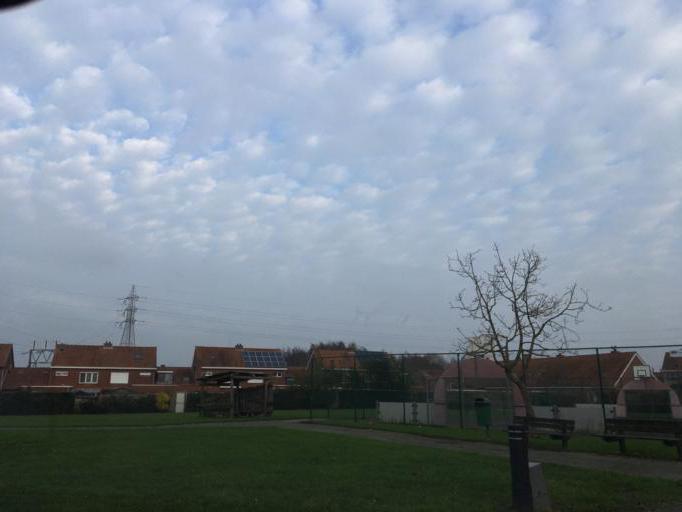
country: BE
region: Flanders
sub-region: Provincie West-Vlaanderen
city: Roeselare
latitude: 50.9336
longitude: 3.1374
